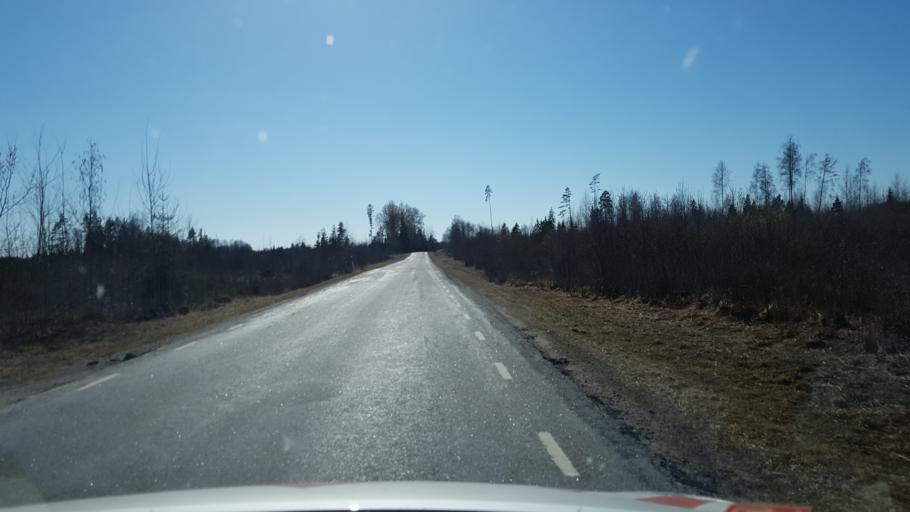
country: EE
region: Laeaene-Virumaa
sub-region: Tamsalu vald
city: Tamsalu
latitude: 59.0766
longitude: 26.1386
